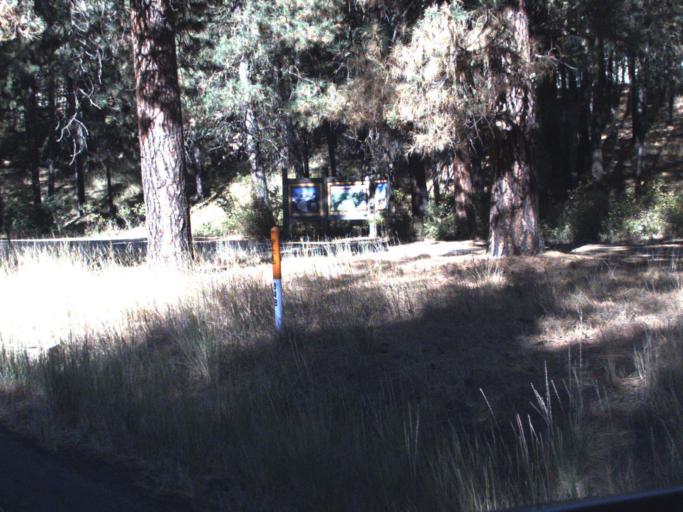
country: US
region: Washington
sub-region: Yakima County
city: Tieton
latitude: 46.6758
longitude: -121.0781
